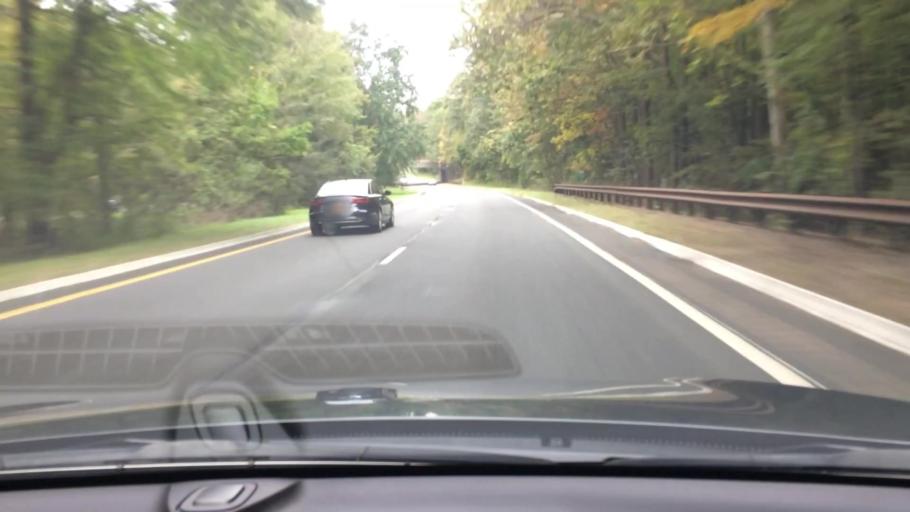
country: US
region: New York
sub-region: Rockland County
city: Sparkill
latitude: 41.0165
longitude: -73.9269
